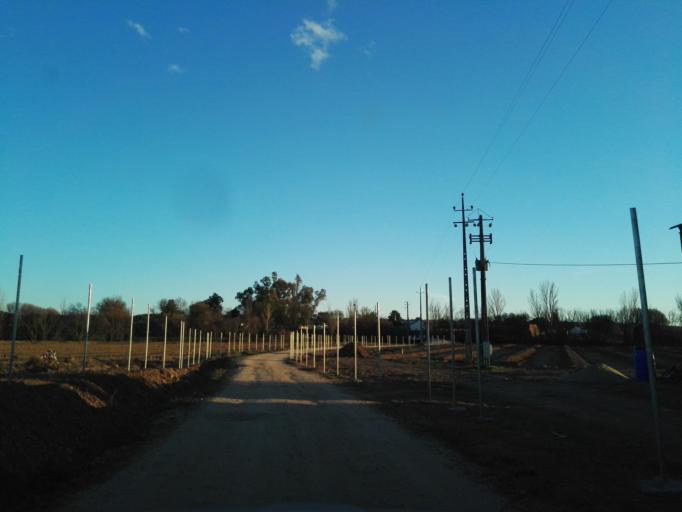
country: PT
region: Castelo Branco
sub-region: Idanha-A-Nova
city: Idanha-a-Nova
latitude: 39.8654
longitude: -7.1355
